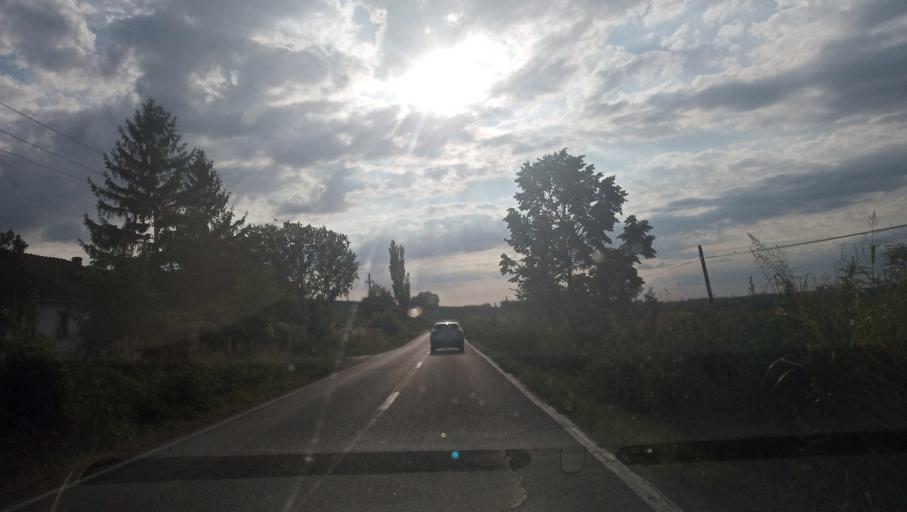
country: BG
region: Silistra
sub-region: Obshtina Silistra
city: Silistra
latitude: 44.1070
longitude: 27.3065
